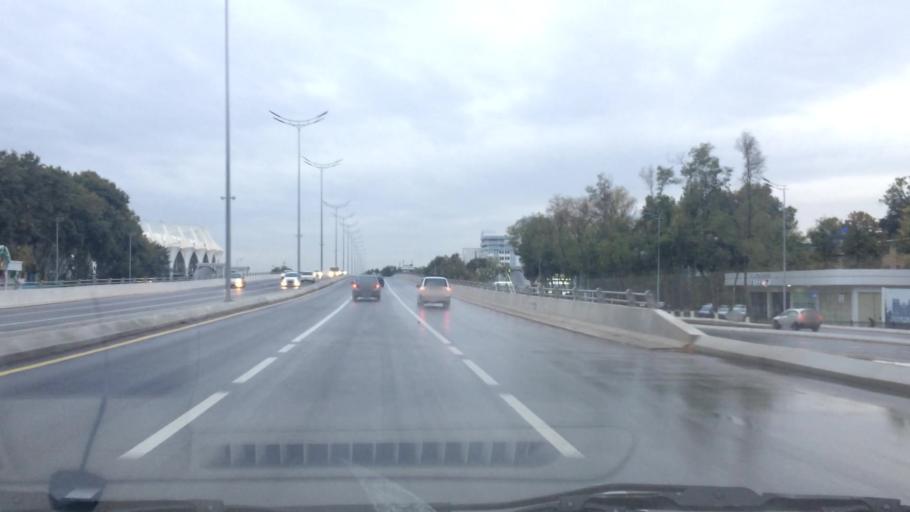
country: UZ
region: Toshkent Shahri
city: Tashkent
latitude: 41.2844
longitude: 69.2147
